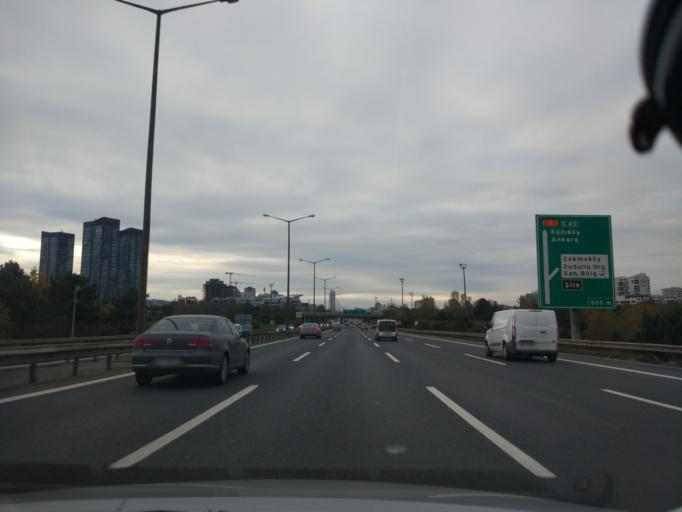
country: TR
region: Istanbul
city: Umraniye
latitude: 41.0338
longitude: 29.1210
